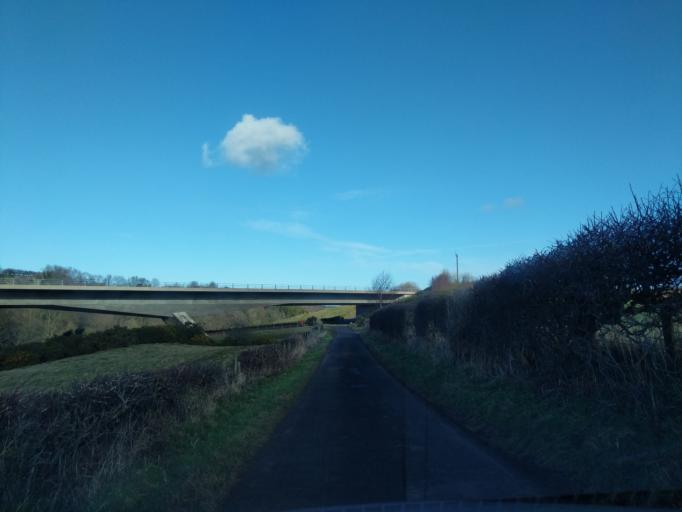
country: GB
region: Scotland
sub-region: East Lothian
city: East Linton
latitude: 55.9763
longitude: -2.6667
